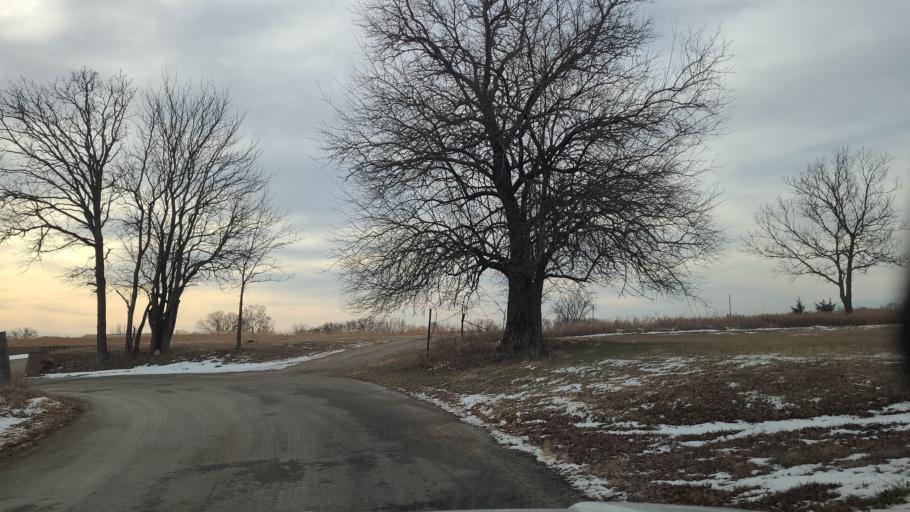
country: US
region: Kansas
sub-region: Douglas County
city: Lawrence
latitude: 39.0372
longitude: -95.3845
